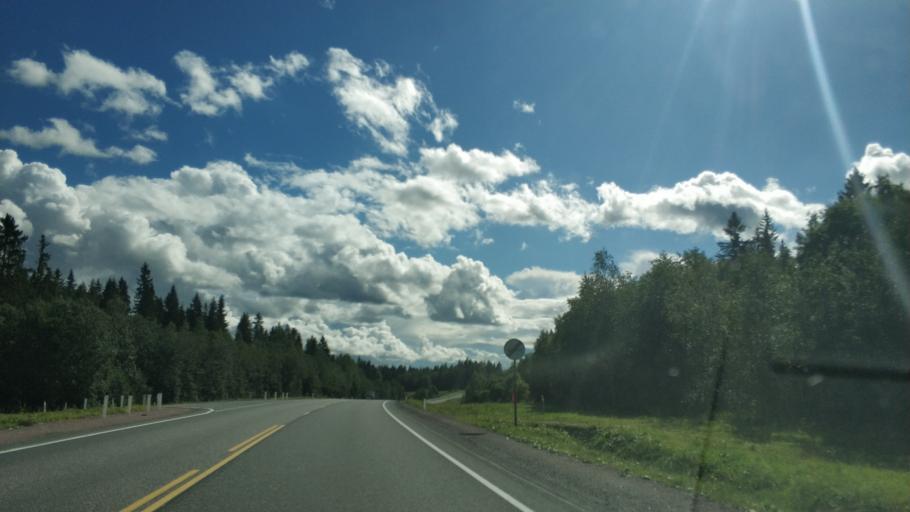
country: RU
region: Republic of Karelia
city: Ruskeala
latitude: 61.8907
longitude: 30.6433
